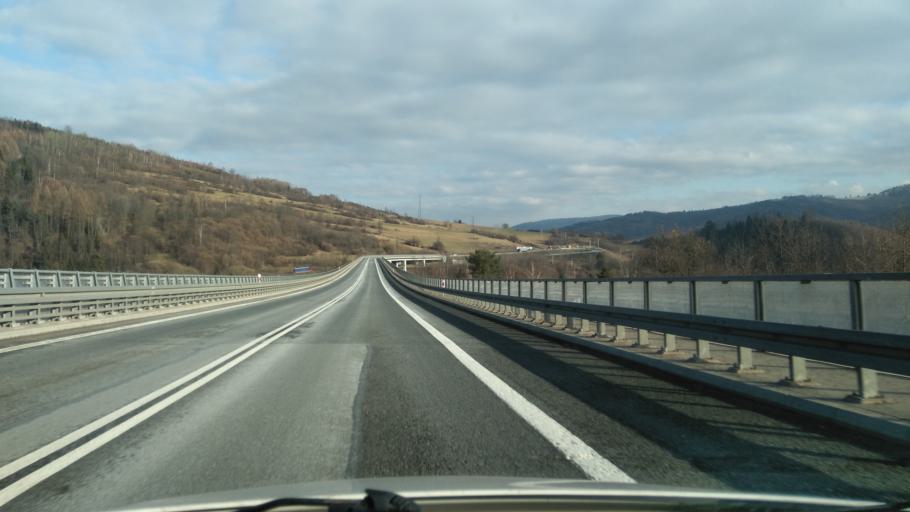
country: PL
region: Silesian Voivodeship
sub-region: Powiat zywiecki
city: Milowka
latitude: 49.5650
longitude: 19.0681
